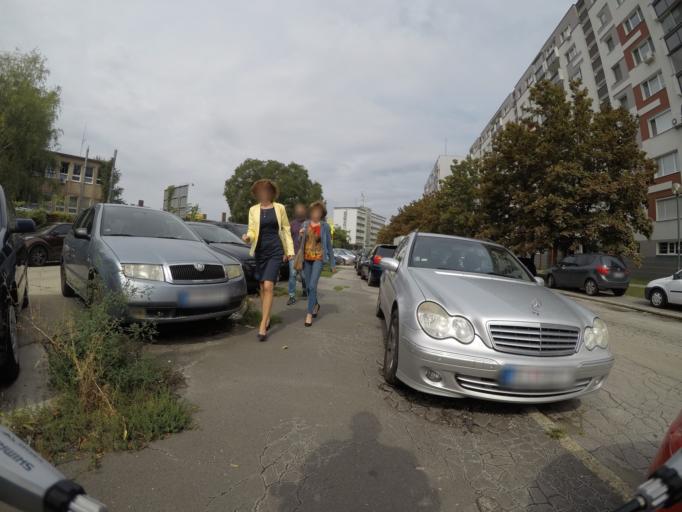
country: SK
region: Bratislavsky
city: Bratislava
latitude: 48.1464
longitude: 17.1591
